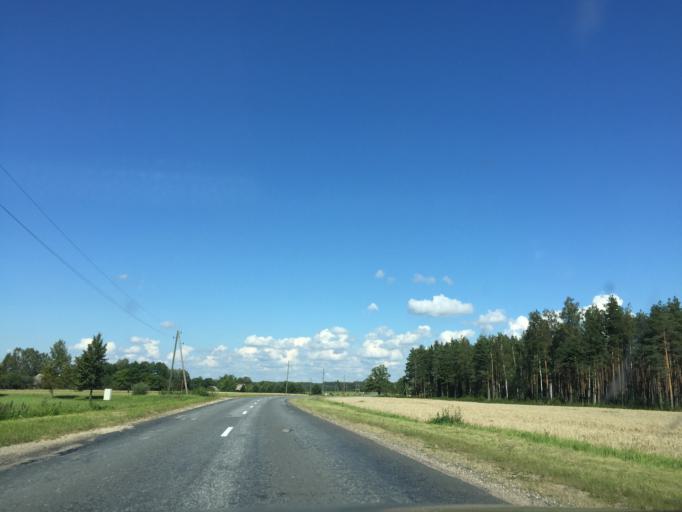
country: LV
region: Limbazu Rajons
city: Limbazi
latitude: 57.4262
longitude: 24.7083
